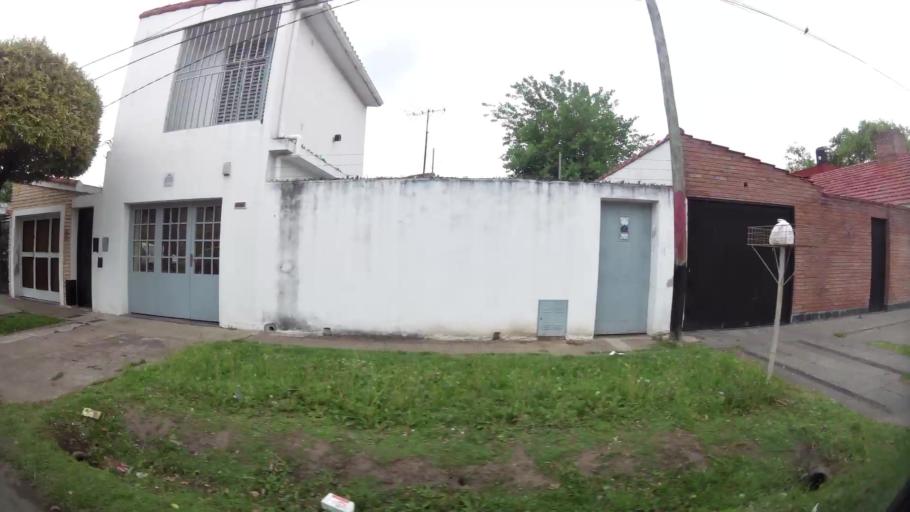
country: AR
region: Santa Fe
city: Gobernador Galvez
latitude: -32.9985
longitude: -60.6712
